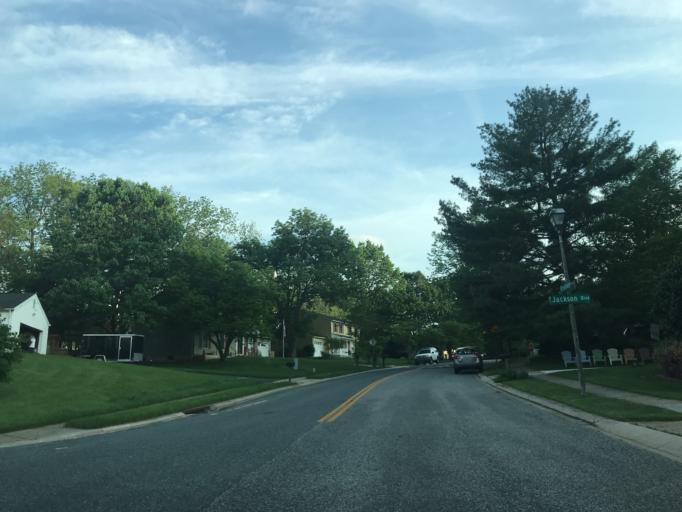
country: US
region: Maryland
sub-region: Harford County
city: South Bel Air
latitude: 39.5430
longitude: -76.3366
